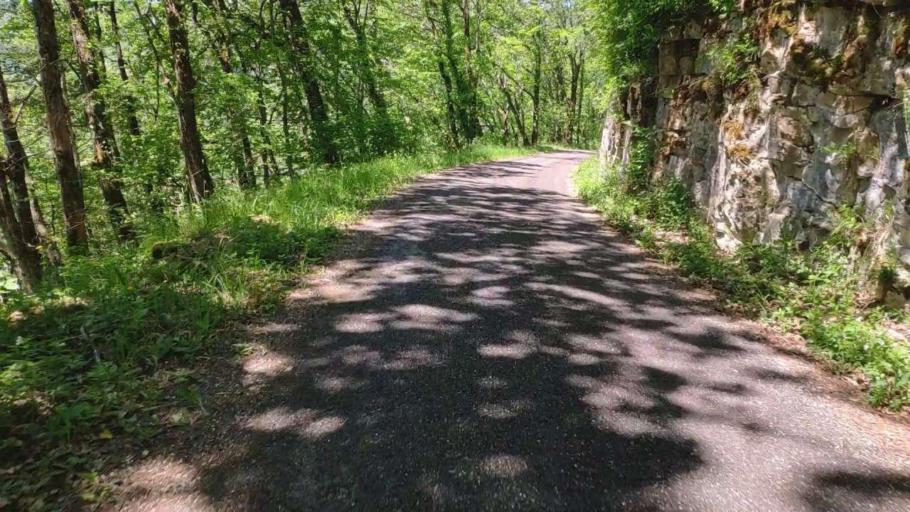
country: FR
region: Franche-Comte
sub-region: Departement du Jura
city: Poligny
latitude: 46.7499
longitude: 5.6786
